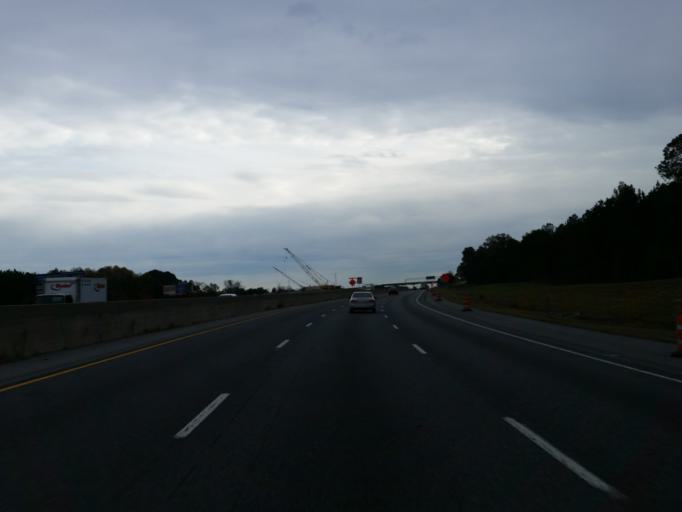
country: US
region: Georgia
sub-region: Tift County
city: Tifton
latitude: 31.5132
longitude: -83.5153
